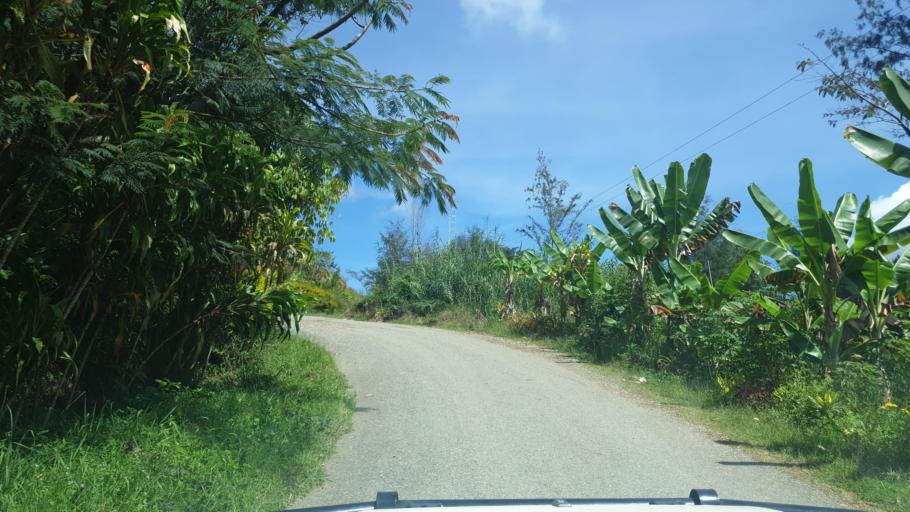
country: PG
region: Chimbu
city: Kundiawa
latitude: -6.1380
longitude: 145.1280
